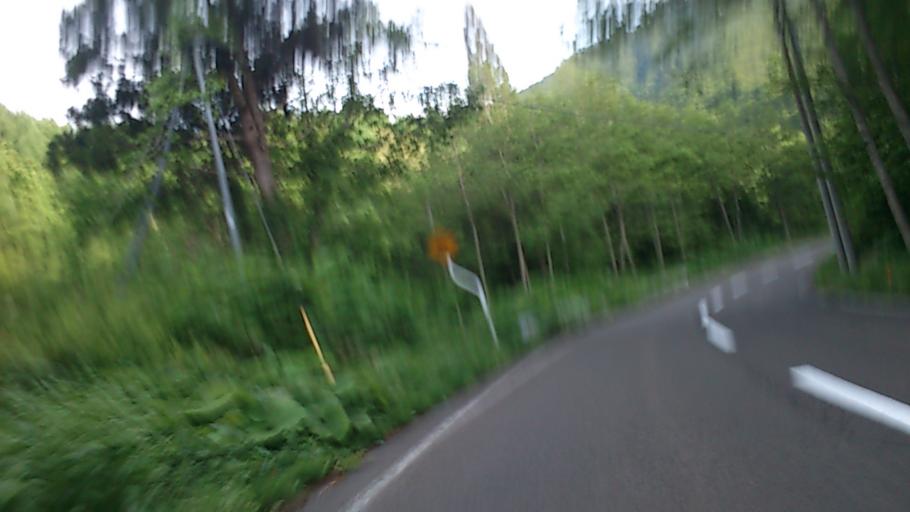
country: JP
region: Aomori
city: Aomori Shi
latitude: 40.6515
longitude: 140.7650
